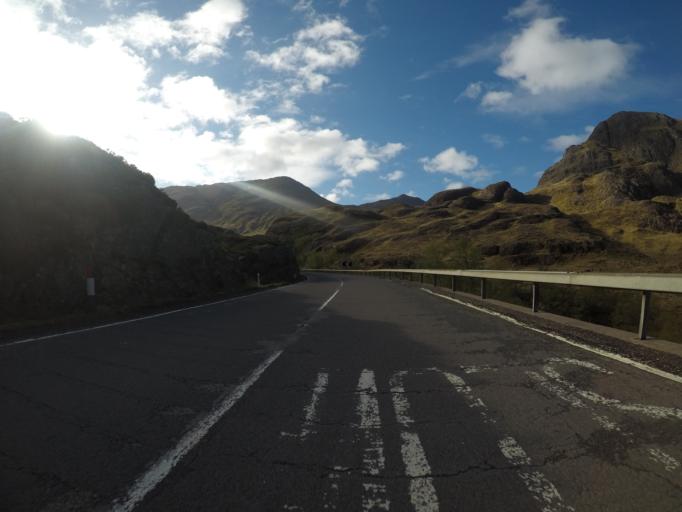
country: GB
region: Scotland
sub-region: Highland
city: Fort William
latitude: 56.6643
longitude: -4.9707
